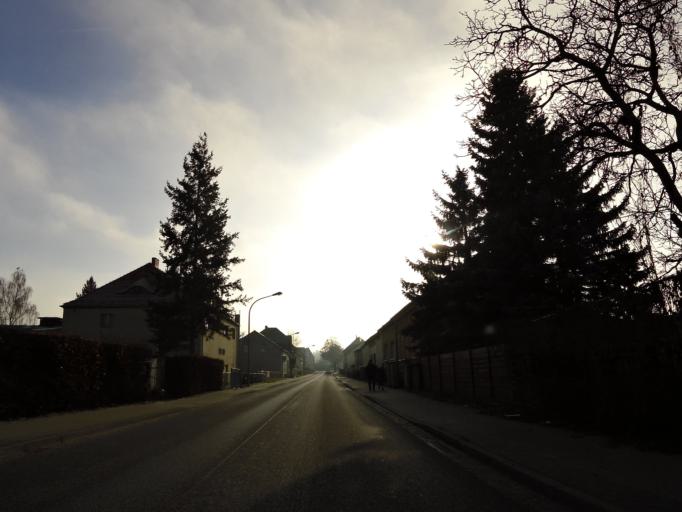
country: DE
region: Brandenburg
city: Werder
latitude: 52.3616
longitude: 12.9091
